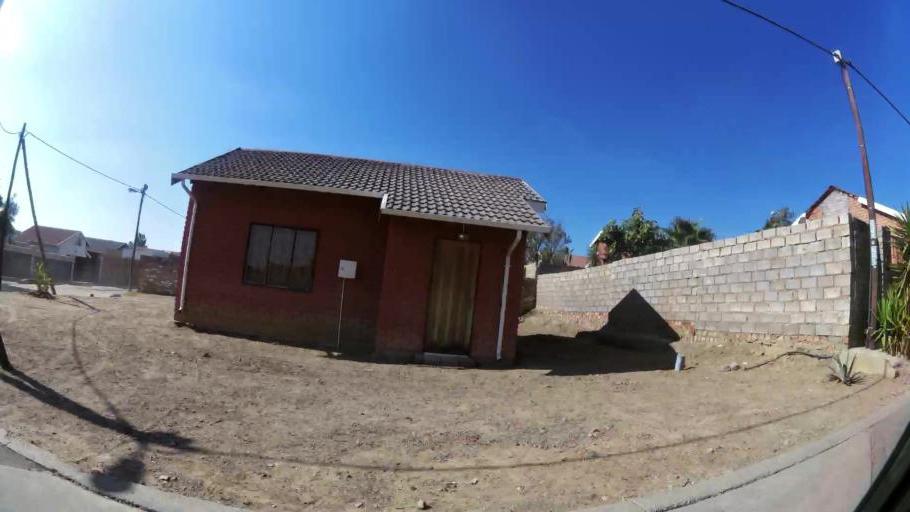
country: ZA
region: Gauteng
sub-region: West Rand District Municipality
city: Muldersdriseloop
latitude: -26.0151
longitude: 27.9340
